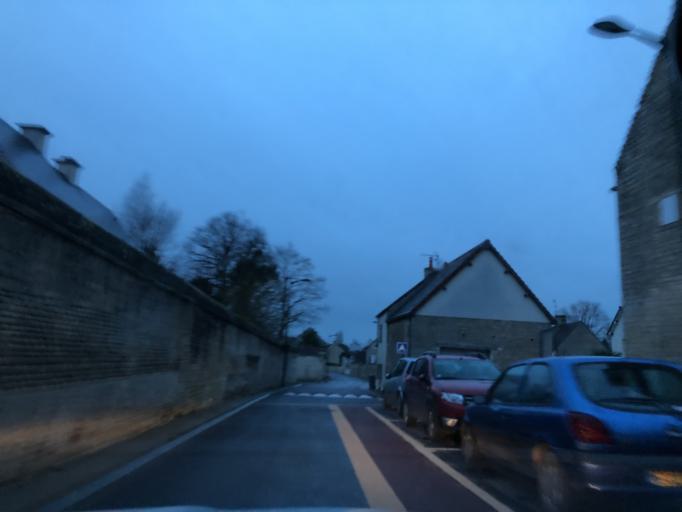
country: FR
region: Lower Normandy
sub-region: Departement du Calvados
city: Mathieu
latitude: 49.2525
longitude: -0.3673
